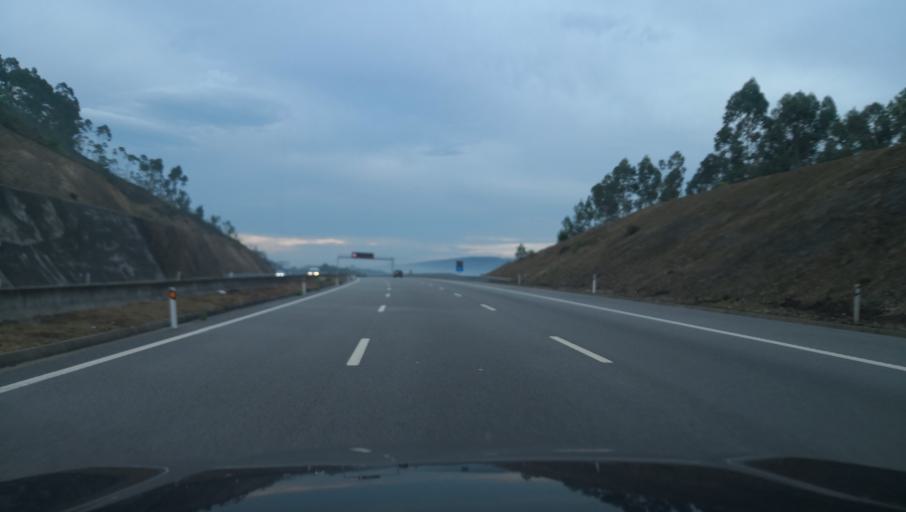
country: PT
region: Porto
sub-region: Paredes
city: Recarei
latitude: 41.1203
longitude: -8.4335
